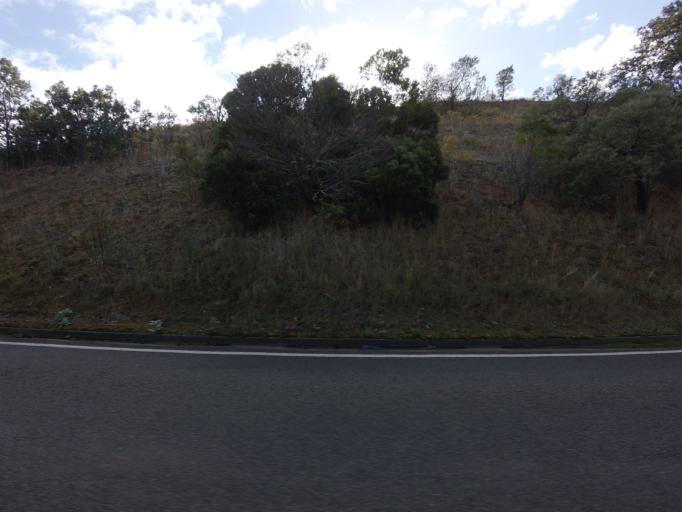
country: AU
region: Tasmania
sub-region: Derwent Valley
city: New Norfolk
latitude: -42.7265
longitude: 146.9545
